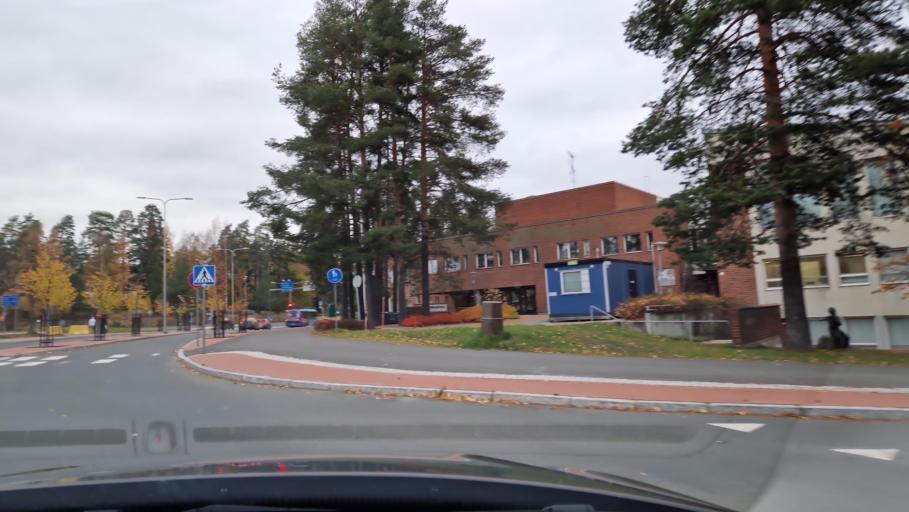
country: FI
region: Northern Savo
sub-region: Kuopio
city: Siilinjaervi
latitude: 63.0751
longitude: 27.6603
